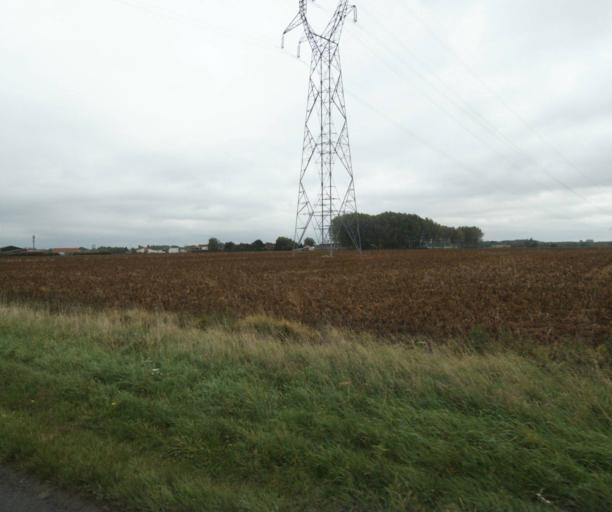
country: FR
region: Nord-Pas-de-Calais
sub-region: Departement du Nord
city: Santes
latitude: 50.5881
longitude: 2.9467
